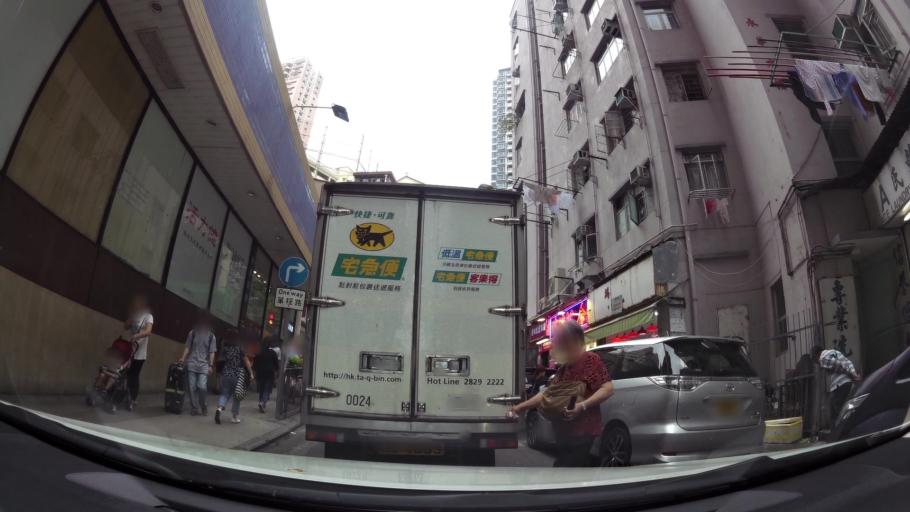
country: HK
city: Hong Kong
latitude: 22.2861
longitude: 114.1370
